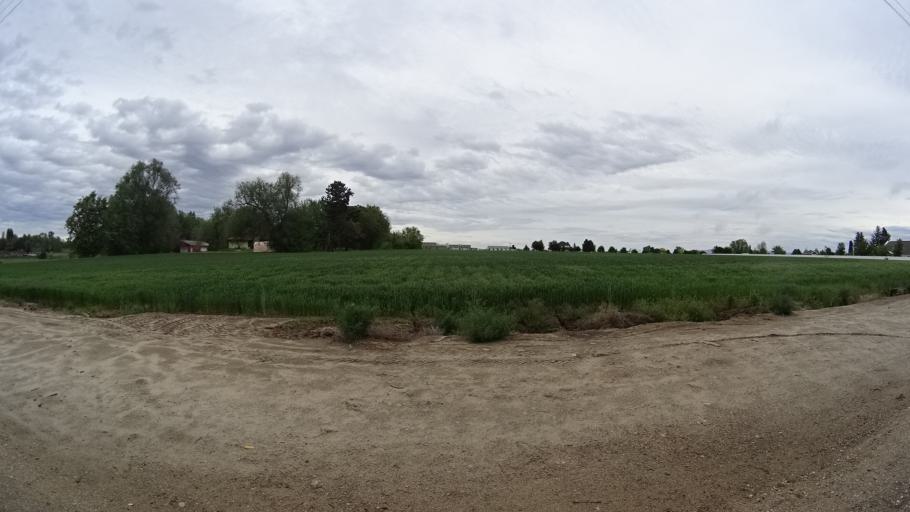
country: US
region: Idaho
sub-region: Ada County
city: Star
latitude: 43.7064
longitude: -116.4729
